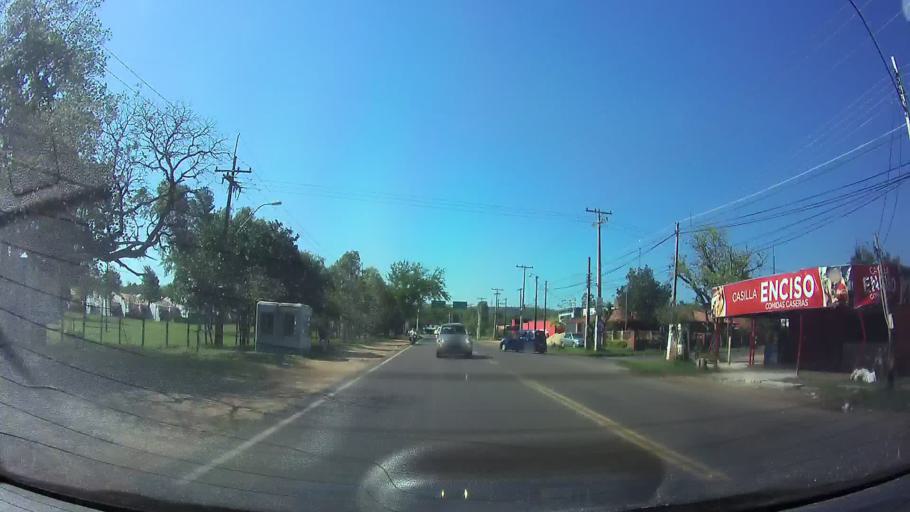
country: PY
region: Cordillera
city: San Bernardino
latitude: -25.3386
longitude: -57.2732
